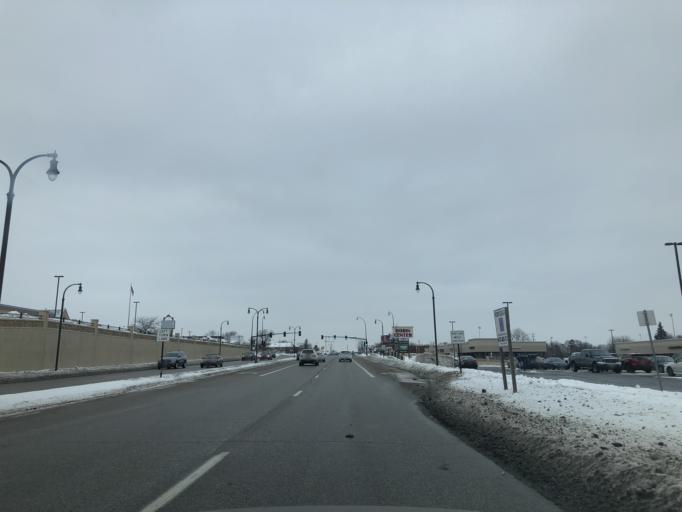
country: US
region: Minnesota
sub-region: Hennepin County
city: Robbinsdale
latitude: 45.0293
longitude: -93.3348
